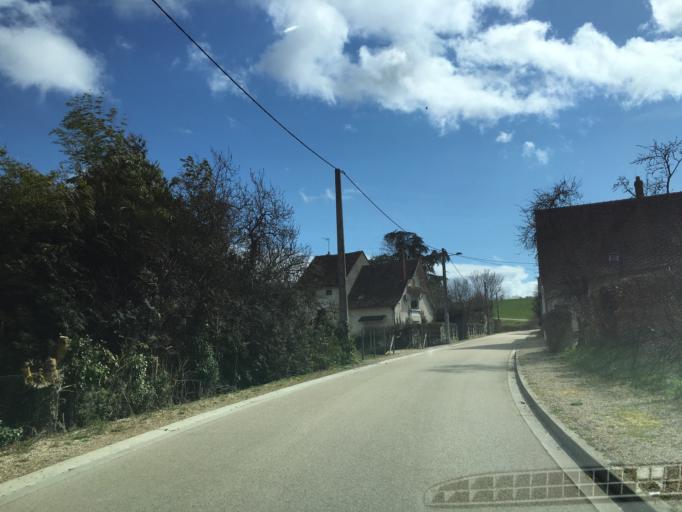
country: FR
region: Bourgogne
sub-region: Departement de l'Yonne
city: Pourrain
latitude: 47.7819
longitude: 3.4066
